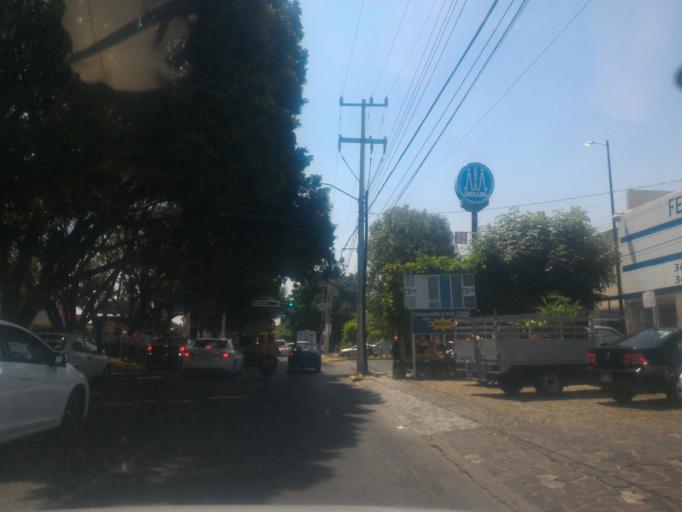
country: MX
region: Jalisco
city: Guadalajara
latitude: 20.6286
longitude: -103.4194
